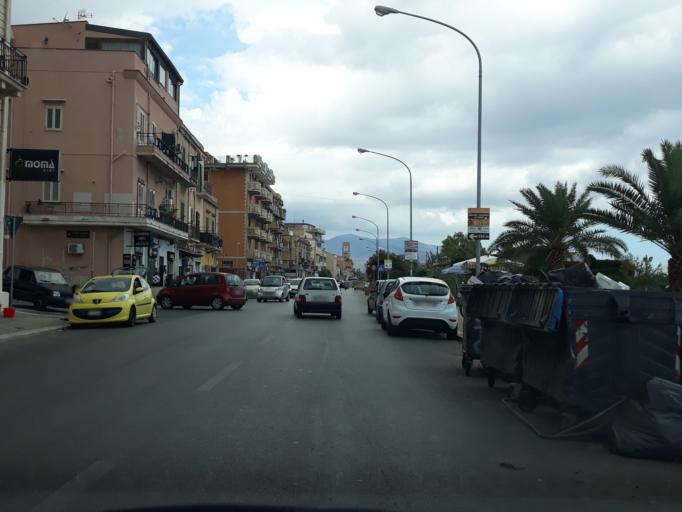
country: IT
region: Sicily
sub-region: Palermo
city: Ciaculli
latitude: 38.1038
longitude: 13.3923
